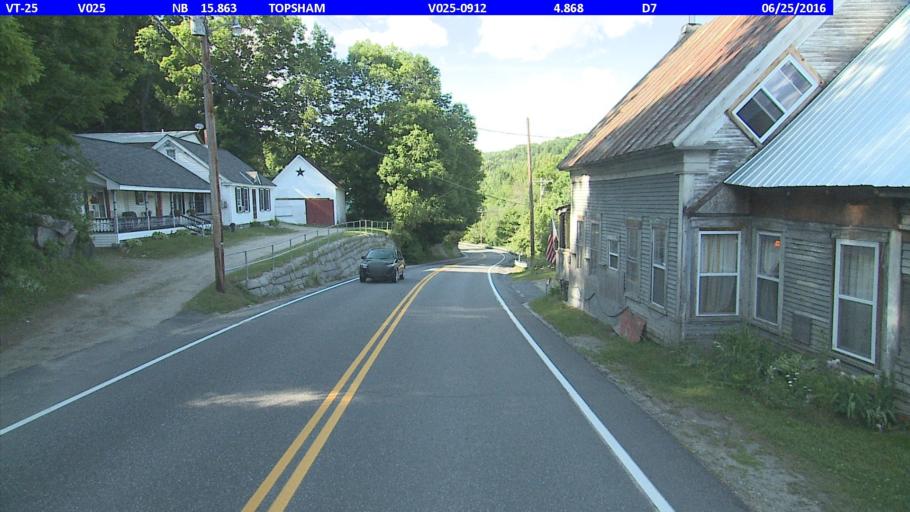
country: US
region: Vermont
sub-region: Orange County
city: Chelsea
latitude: 44.1172
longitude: -72.3083
